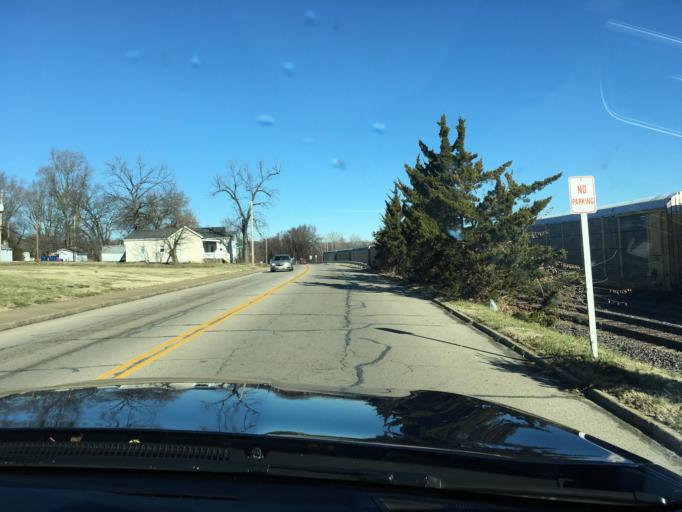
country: US
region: Missouri
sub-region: Jefferson County
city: De Soto
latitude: 38.1453
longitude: -90.5513
